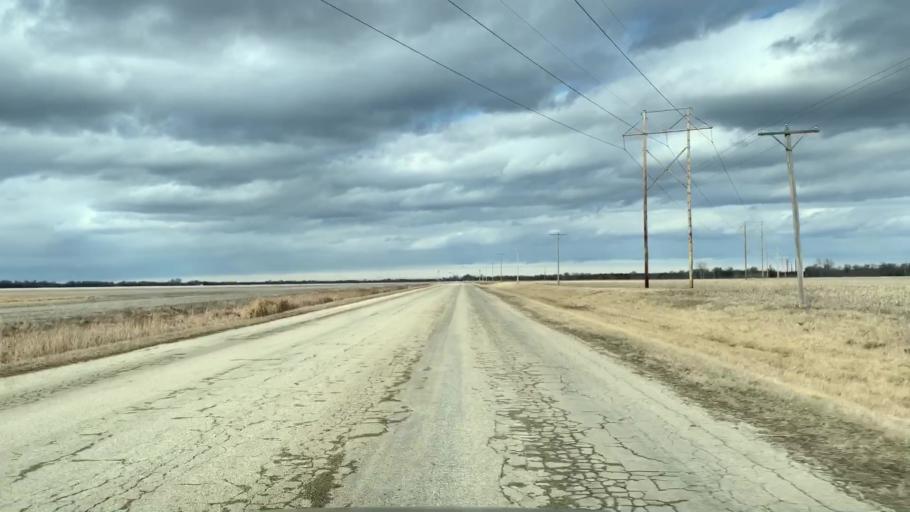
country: US
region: Kansas
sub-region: Allen County
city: Humboldt
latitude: 37.7702
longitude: -95.4706
